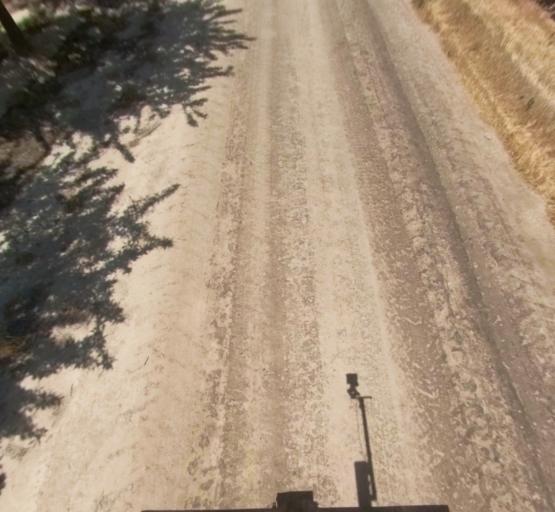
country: US
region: California
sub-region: Fresno County
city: Kerman
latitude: 36.8221
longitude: -120.1856
